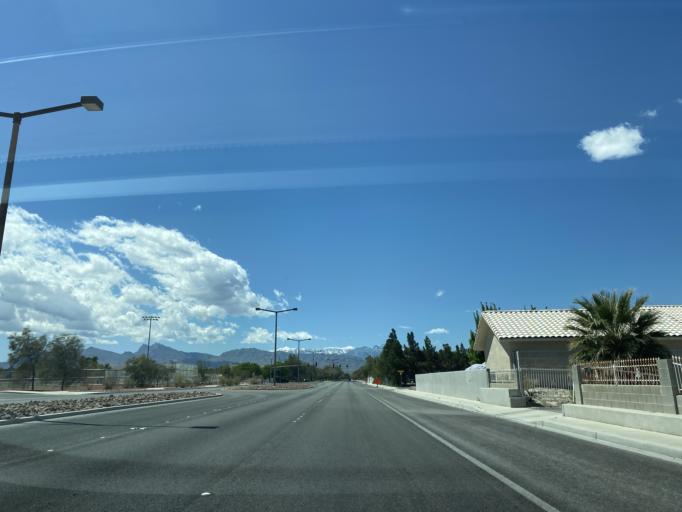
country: US
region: Nevada
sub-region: Clark County
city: North Las Vegas
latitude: 36.3058
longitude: -115.2130
